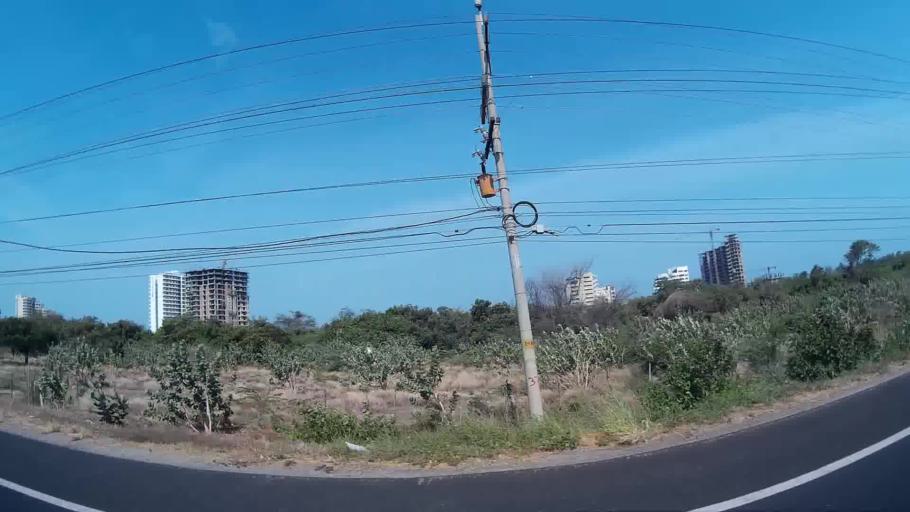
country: CO
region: Magdalena
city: Santa Marta
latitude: 11.1528
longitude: -74.2224
